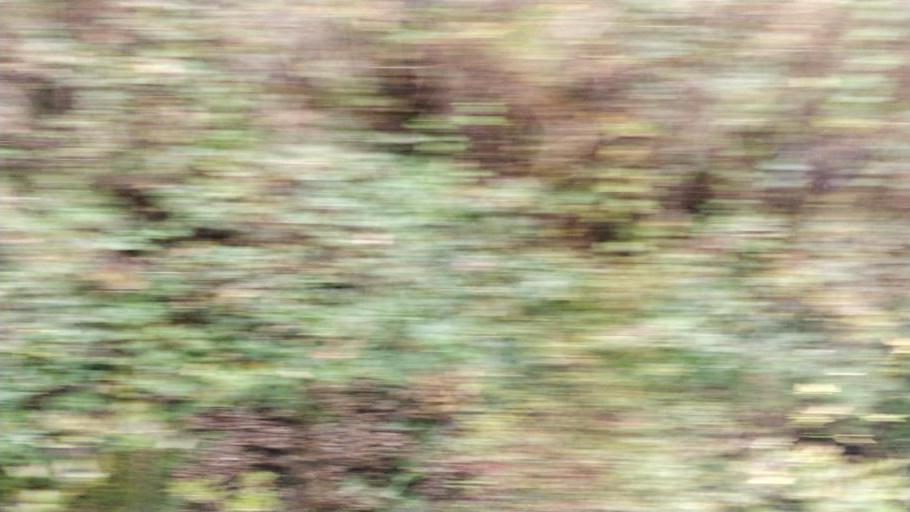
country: GB
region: England
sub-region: Borough of Wigan
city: Hindley
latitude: 53.5427
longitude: -2.5721
